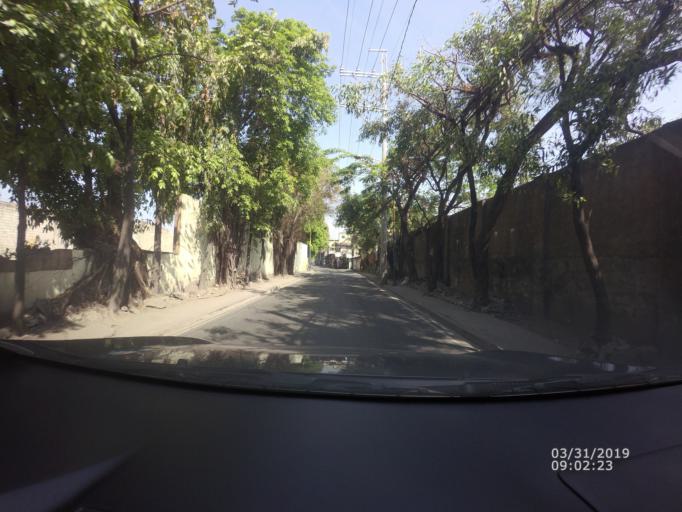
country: PH
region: Metro Manila
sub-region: Mandaluyong
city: Mandaluyong City
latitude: 14.5773
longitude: 121.0227
